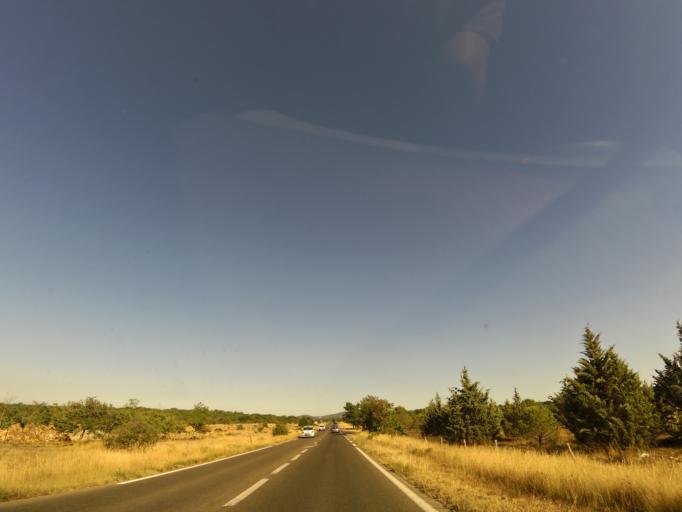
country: FR
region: Languedoc-Roussillon
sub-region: Departement du Gard
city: Saint-Hippolyte-du-Fort
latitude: 43.9524
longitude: 3.8786
